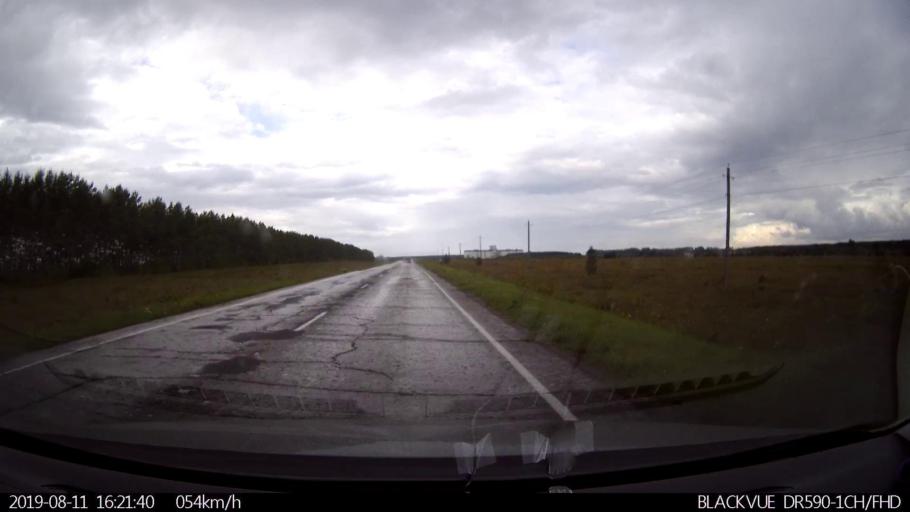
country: RU
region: Ulyanovsk
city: Mayna
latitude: 54.0816
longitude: 47.5969
